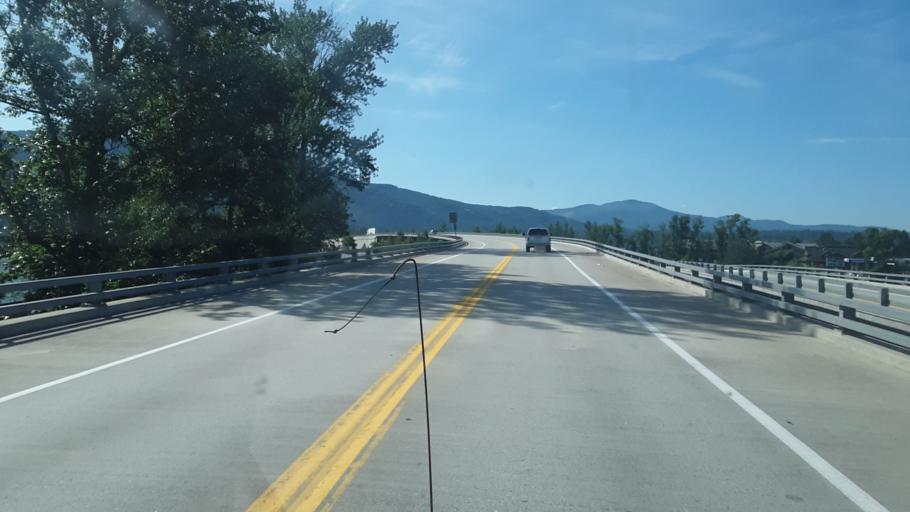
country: US
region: Idaho
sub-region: Bonner County
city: Sandpoint
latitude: 48.2730
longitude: -116.5448
